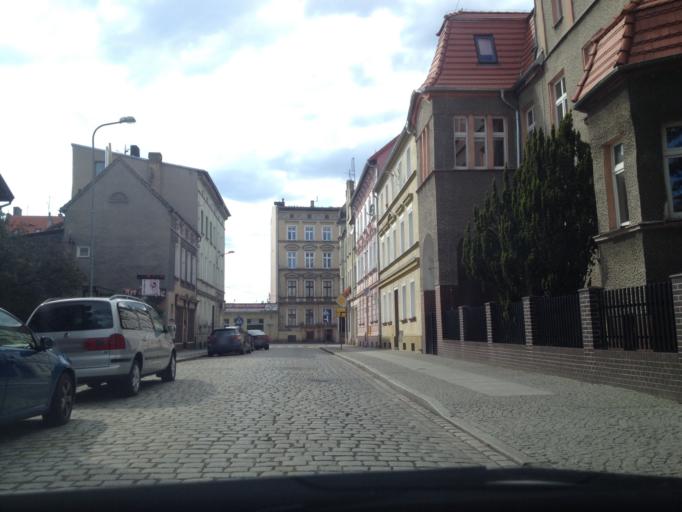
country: PL
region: Lubusz
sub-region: Powiat zarski
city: Zary
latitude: 51.6362
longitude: 15.1387
